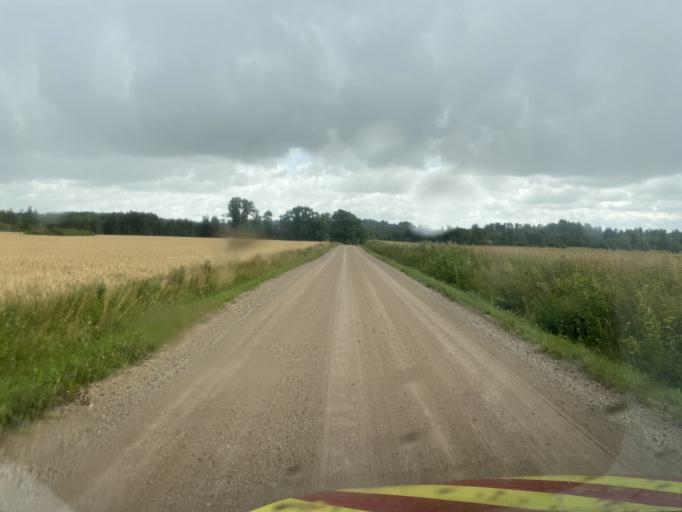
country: EE
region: Valgamaa
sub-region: Torva linn
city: Torva
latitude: 58.1173
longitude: 25.8198
